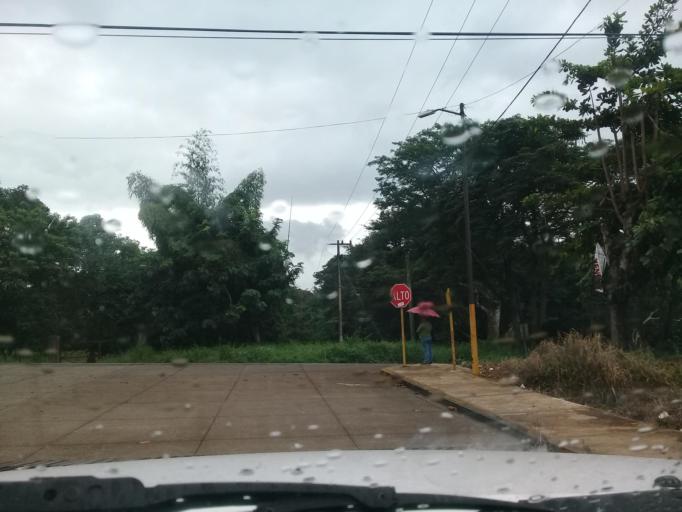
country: MX
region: Veracruz
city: San Andres Tuxtla
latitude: 18.4357
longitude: -95.1928
